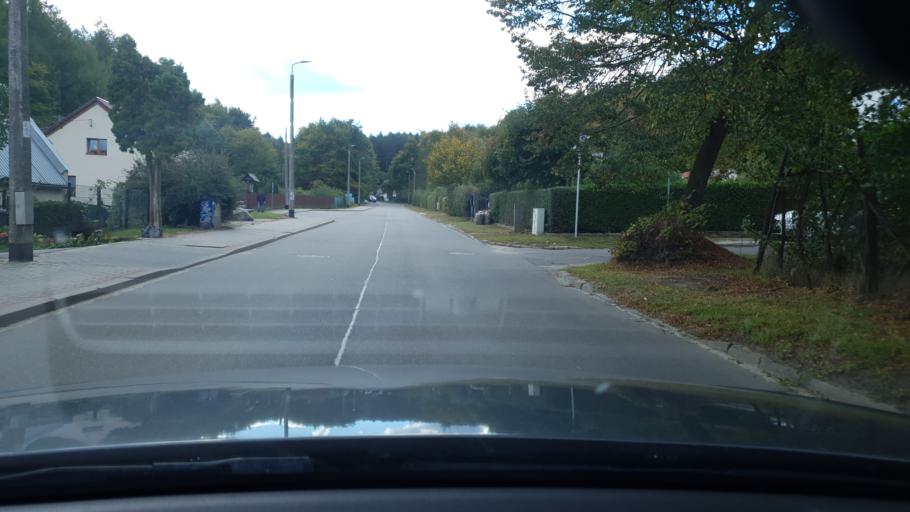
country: PL
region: Pomeranian Voivodeship
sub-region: Powiat wejherowski
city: Reda
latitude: 54.5944
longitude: 18.3392
